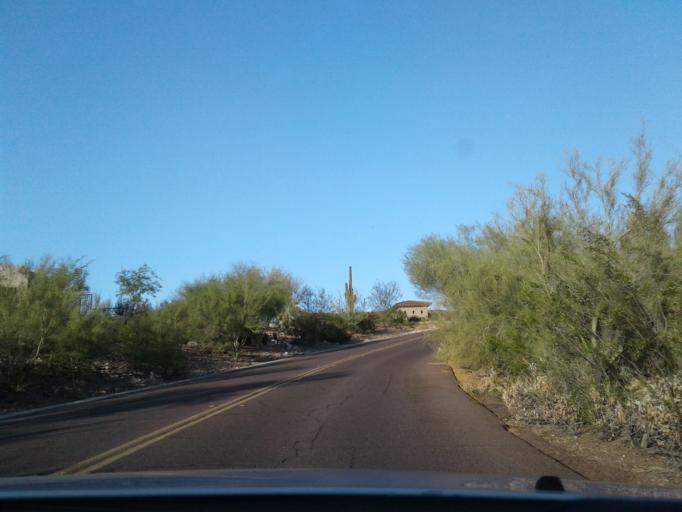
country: US
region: Arizona
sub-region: Maricopa County
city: Paradise Valley
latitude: 33.5276
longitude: -111.9919
